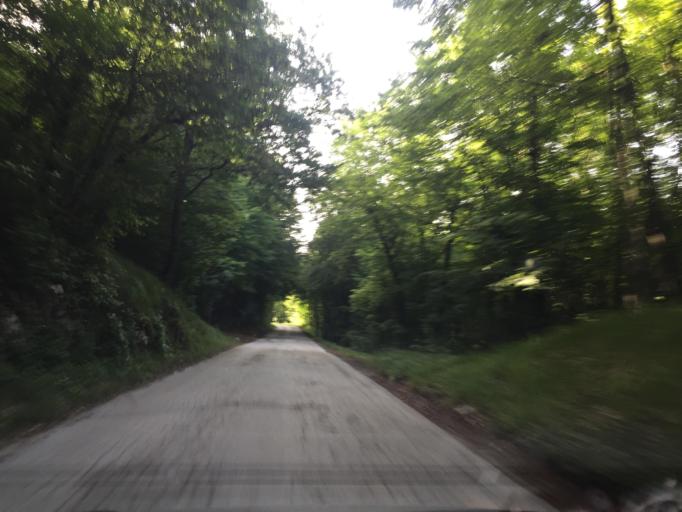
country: HR
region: Istarska
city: Buzet
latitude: 45.4714
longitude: 14.1063
